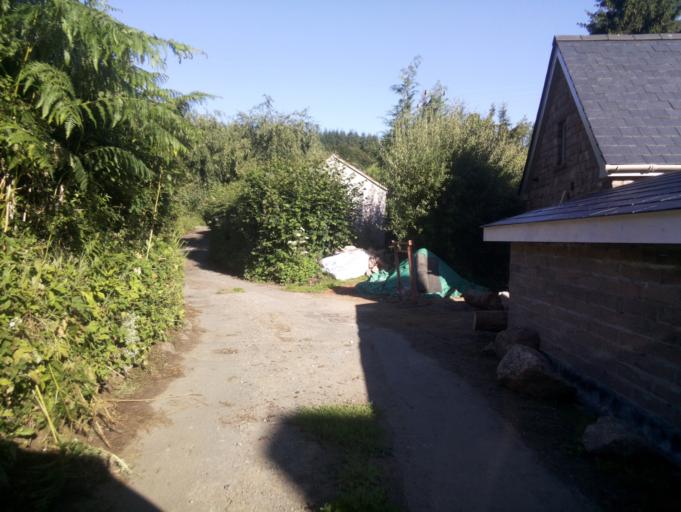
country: GB
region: Wales
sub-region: Monmouthshire
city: Tintern
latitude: 51.6863
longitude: -2.7337
